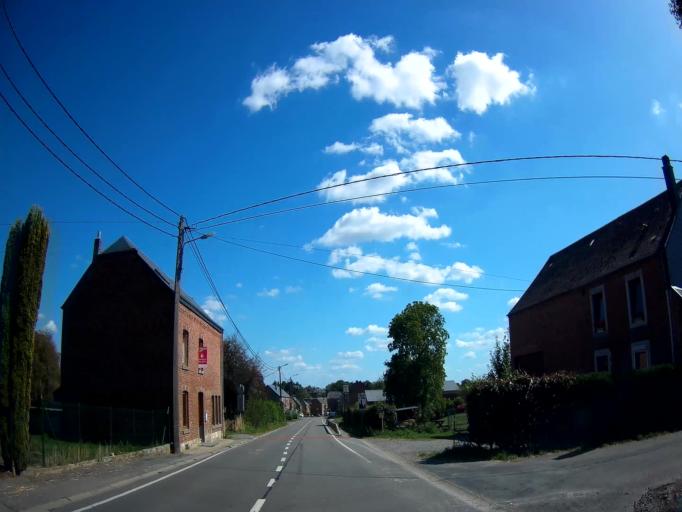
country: FR
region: Champagne-Ardenne
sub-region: Departement des Ardennes
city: Fromelennes
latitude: 50.1703
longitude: 4.8805
